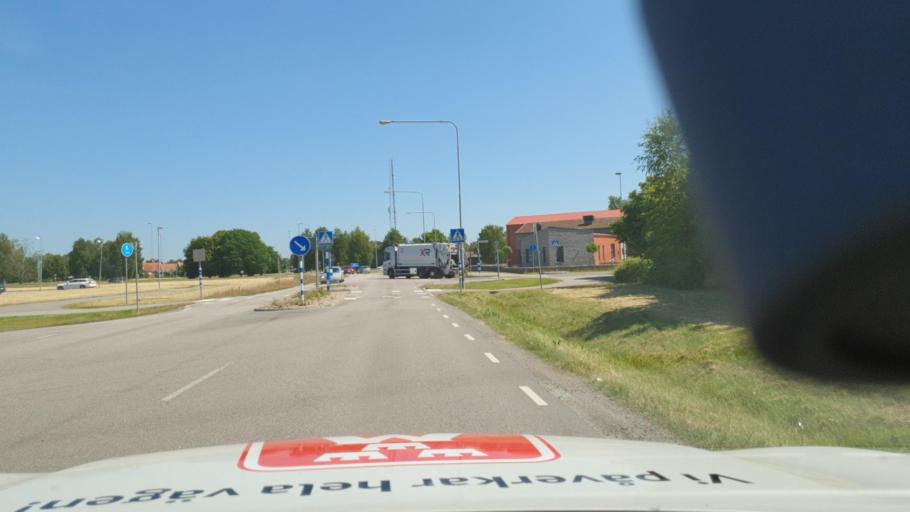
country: SE
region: Vaestra Goetaland
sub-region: Lidkopings Kommun
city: Lidkoping
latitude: 58.5024
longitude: 13.1219
